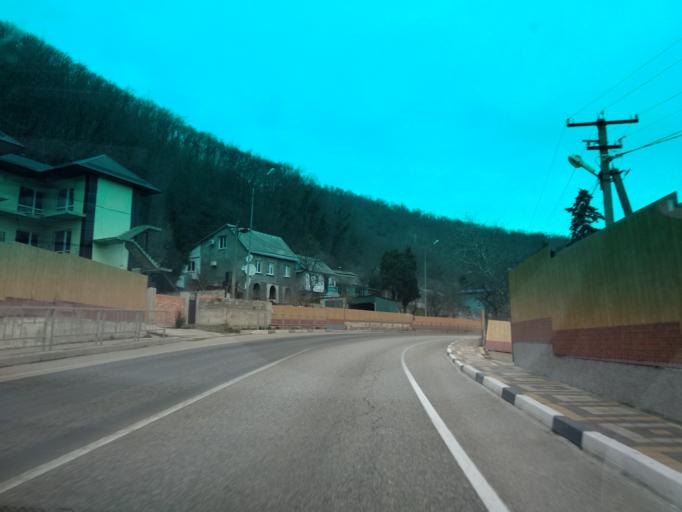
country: RU
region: Krasnodarskiy
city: Ol'ginka
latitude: 44.2024
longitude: 38.8866
